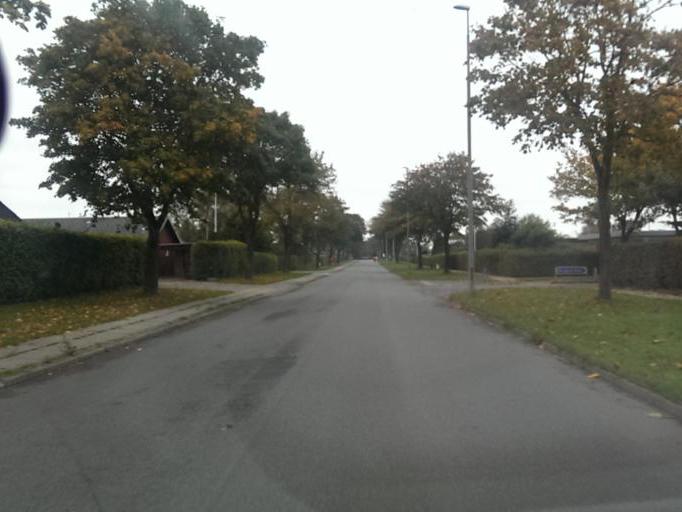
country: DK
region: South Denmark
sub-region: Esbjerg Kommune
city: Bramming
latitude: 55.4669
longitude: 8.7138
